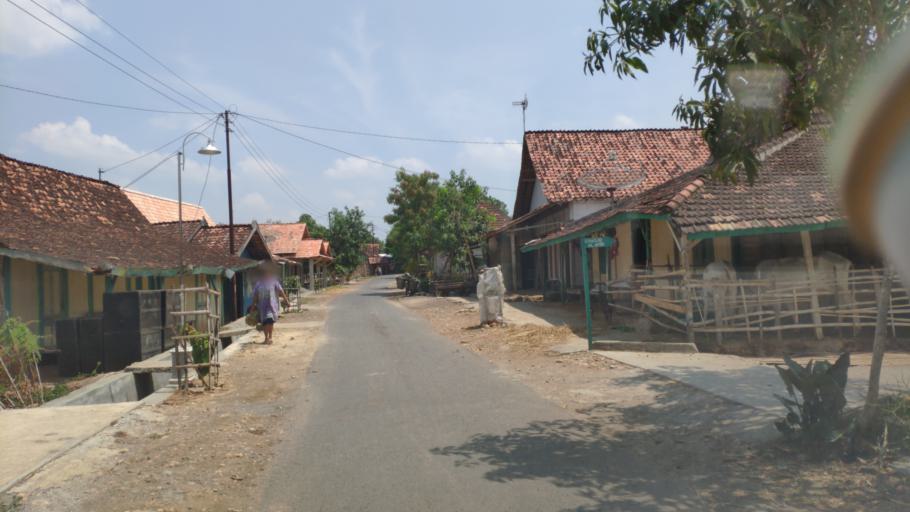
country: ID
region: Central Java
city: Padaan
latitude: -6.9437
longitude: 111.2989
